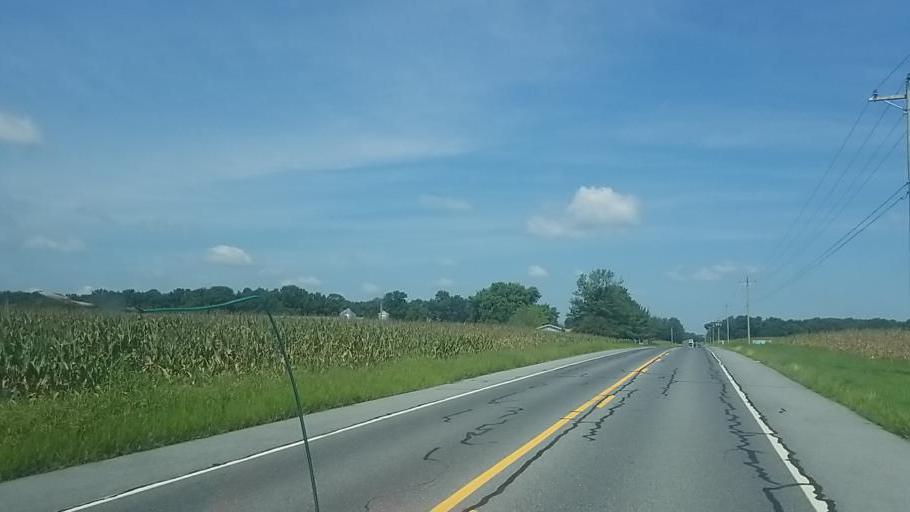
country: US
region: Delaware
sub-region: Sussex County
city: Seaford
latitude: 38.6764
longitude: -75.5783
